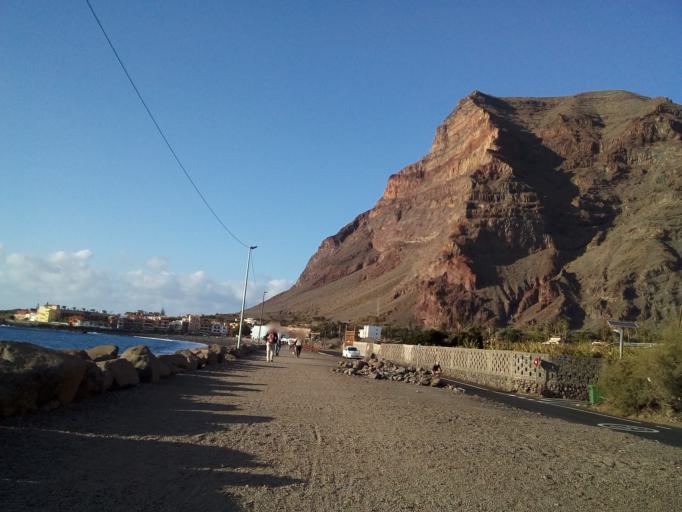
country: ES
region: Canary Islands
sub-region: Provincia de Santa Cruz de Tenerife
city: Alajero
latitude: 28.0905
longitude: -17.3397
